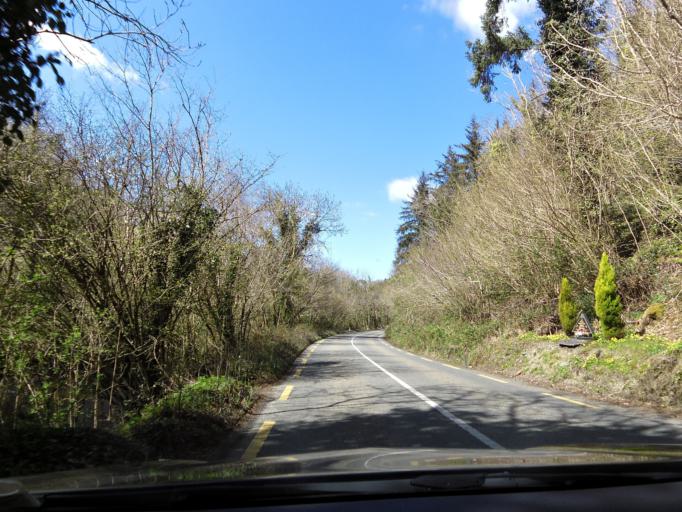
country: IE
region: Leinster
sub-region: Wicklow
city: Aughrim
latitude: 52.8442
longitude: -6.2657
